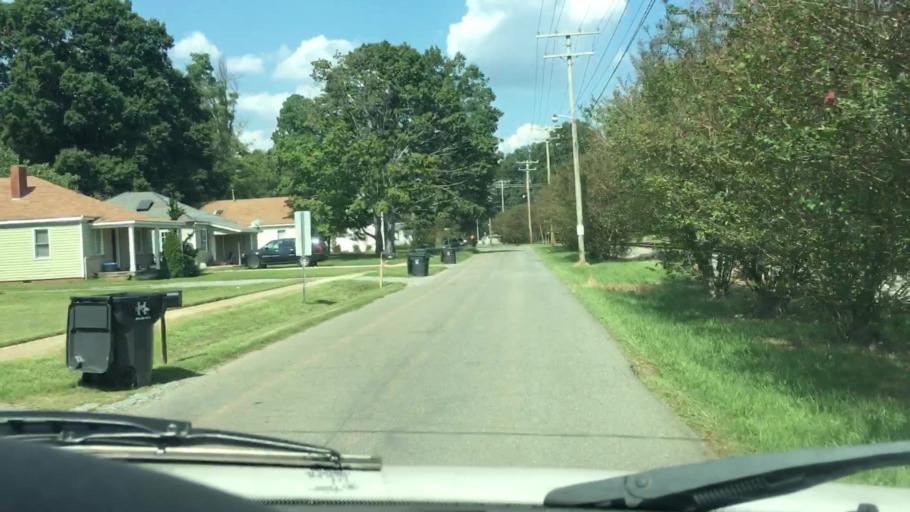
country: US
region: North Carolina
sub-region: Mecklenburg County
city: Huntersville
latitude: 35.4165
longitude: -80.8406
